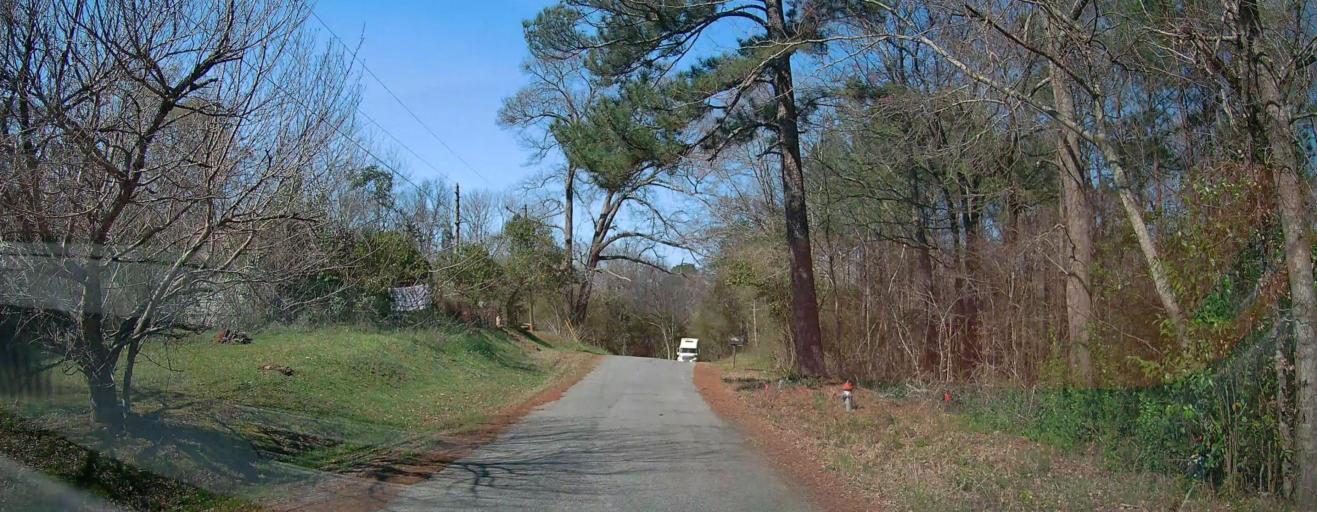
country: US
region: Georgia
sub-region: Jones County
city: Gray
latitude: 33.0052
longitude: -83.5608
